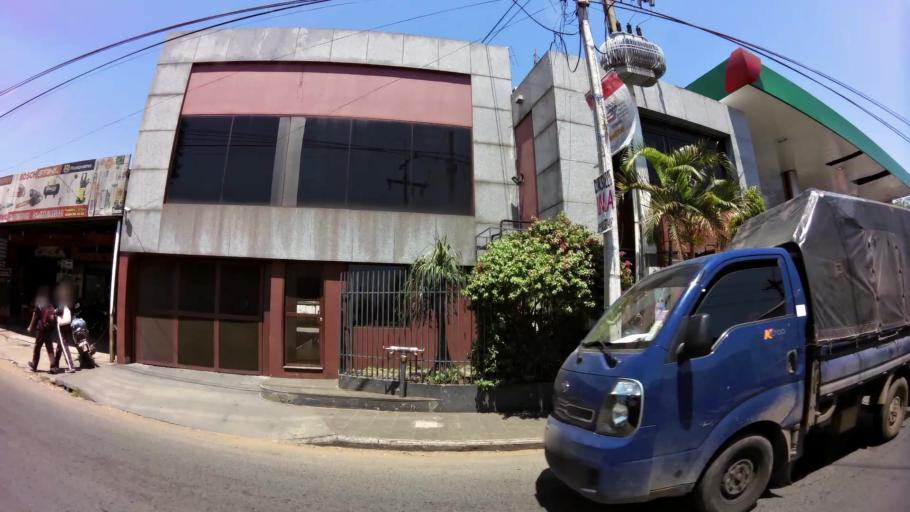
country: PY
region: Central
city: Nemby
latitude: -25.3943
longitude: -57.5440
